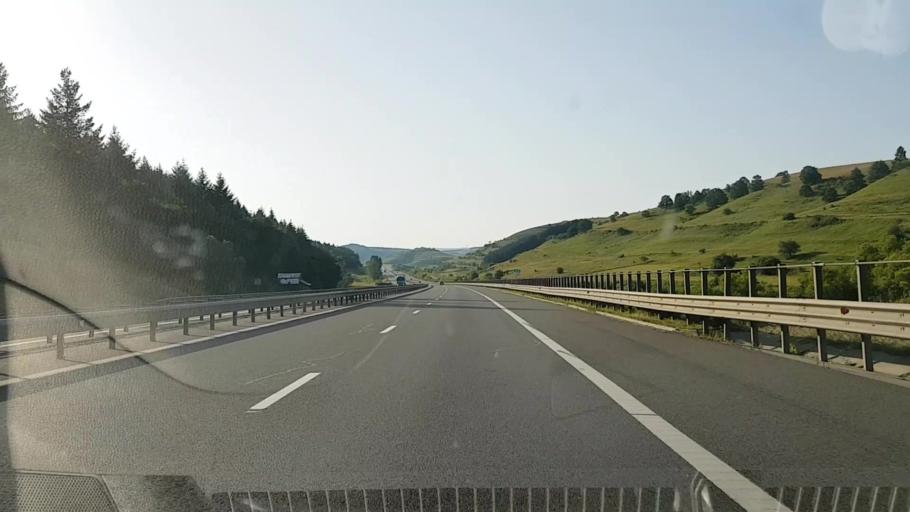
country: RO
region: Cluj
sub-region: Comuna Savadisla
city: Savadisla
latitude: 46.6713
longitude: 23.4839
